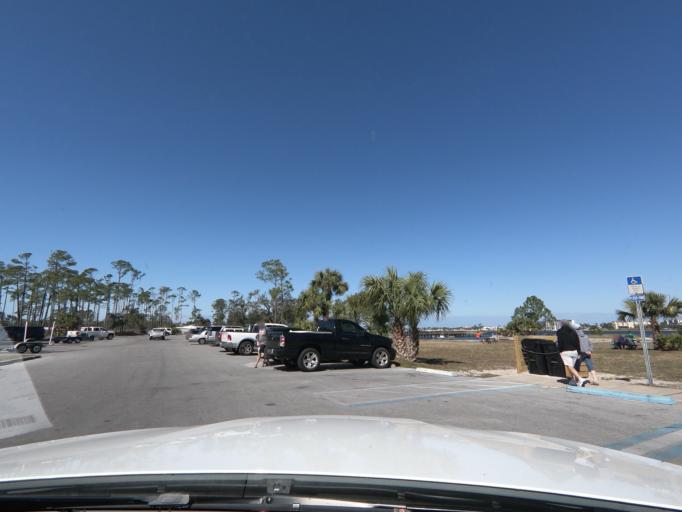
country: US
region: Florida
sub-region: Bay County
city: Lower Grand Lagoon
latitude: 30.1320
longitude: -85.7311
